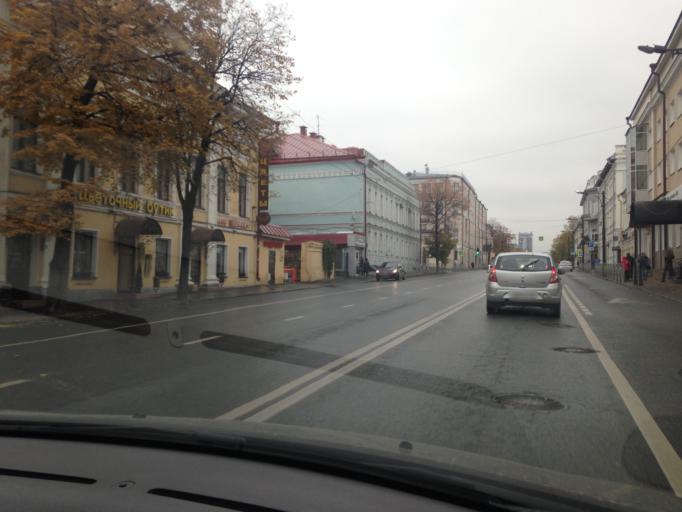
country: RU
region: Tatarstan
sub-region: Gorod Kazan'
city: Kazan
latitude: 55.7959
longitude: 49.1279
